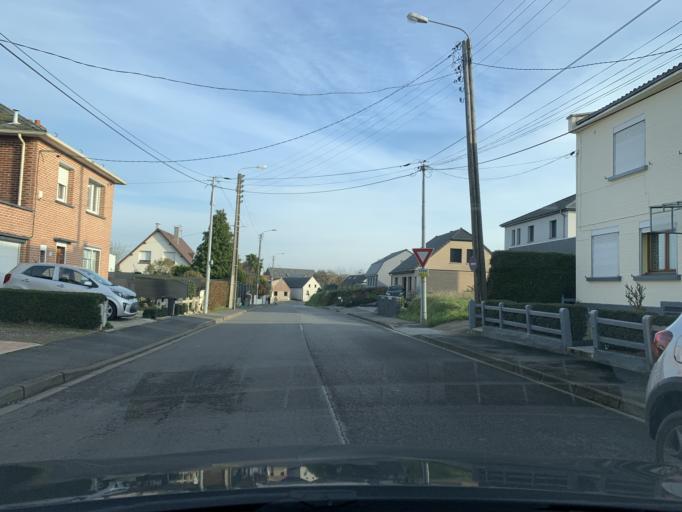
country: FR
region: Nord-Pas-de-Calais
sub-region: Departement du Nord
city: Cambrai
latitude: 50.1592
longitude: 3.2396
